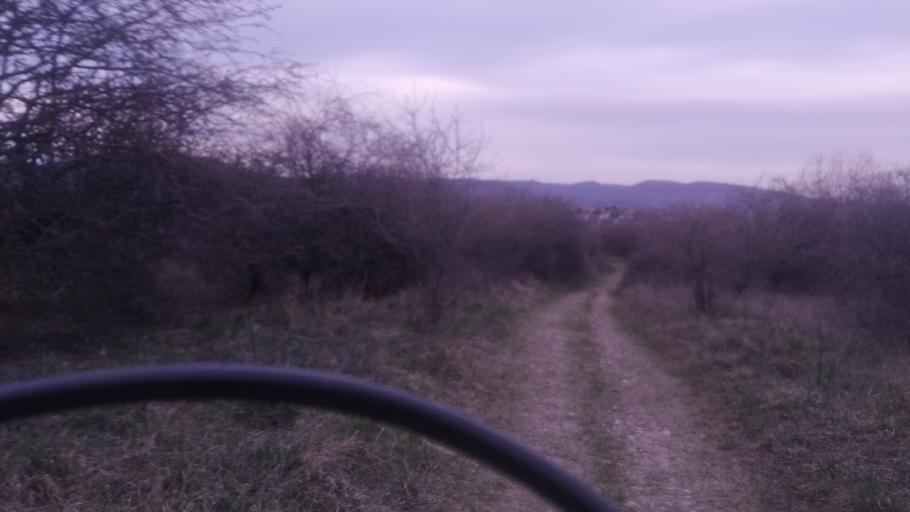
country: HU
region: Pest
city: Pomaz
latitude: 47.6227
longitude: 19.0189
